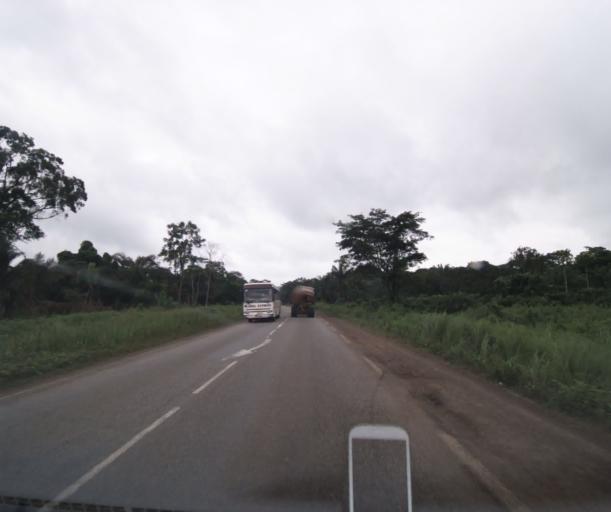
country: CM
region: Littoral
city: Edea
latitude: 3.8123
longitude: 10.3041
